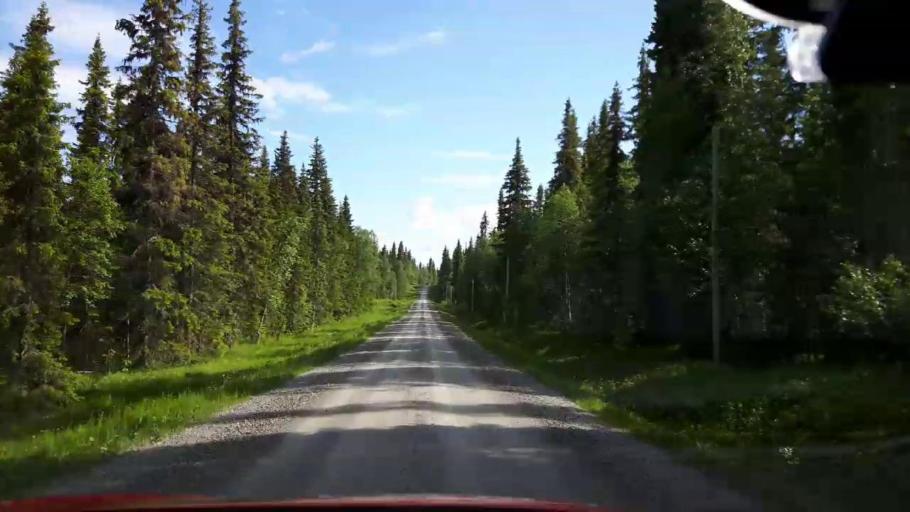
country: SE
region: Jaemtland
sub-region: Krokoms Kommun
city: Valla
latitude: 63.7980
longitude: 14.0459
